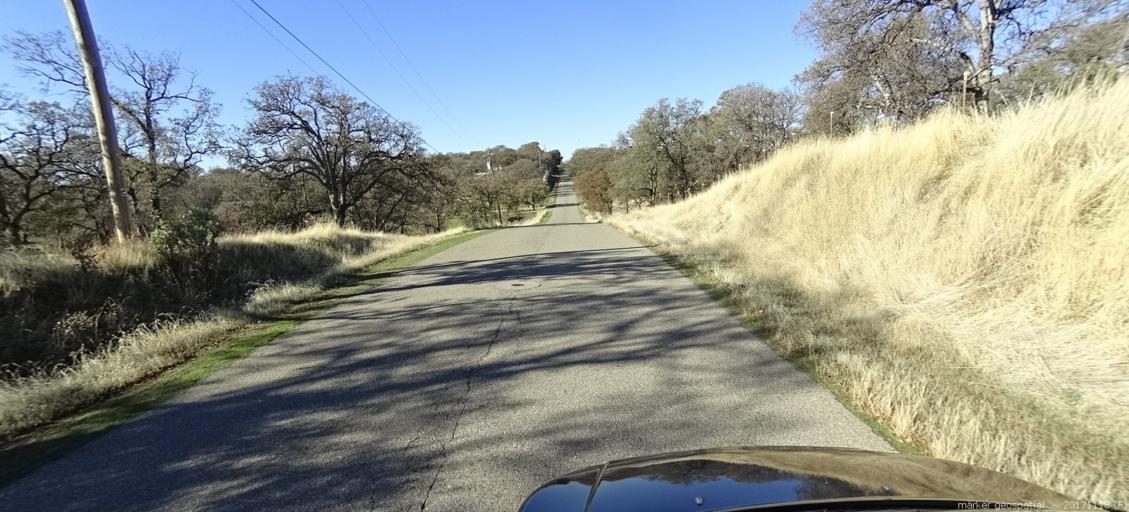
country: US
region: California
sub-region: Shasta County
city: Cottonwood
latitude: 40.3949
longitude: -122.3159
